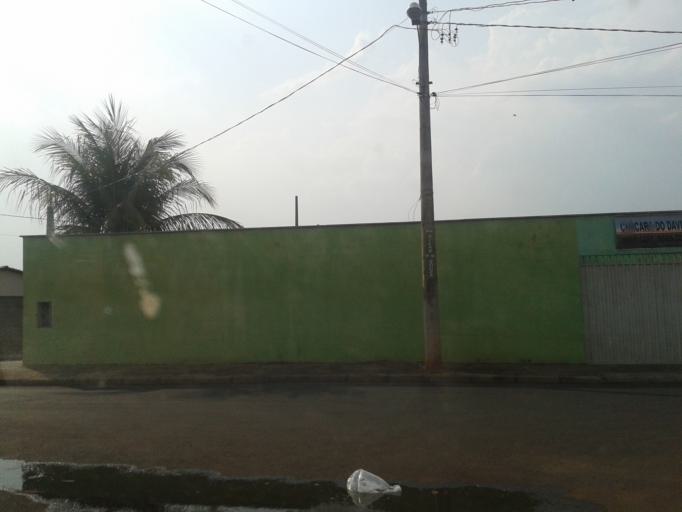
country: BR
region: Minas Gerais
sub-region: Ituiutaba
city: Ituiutaba
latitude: -18.9782
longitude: -49.4840
